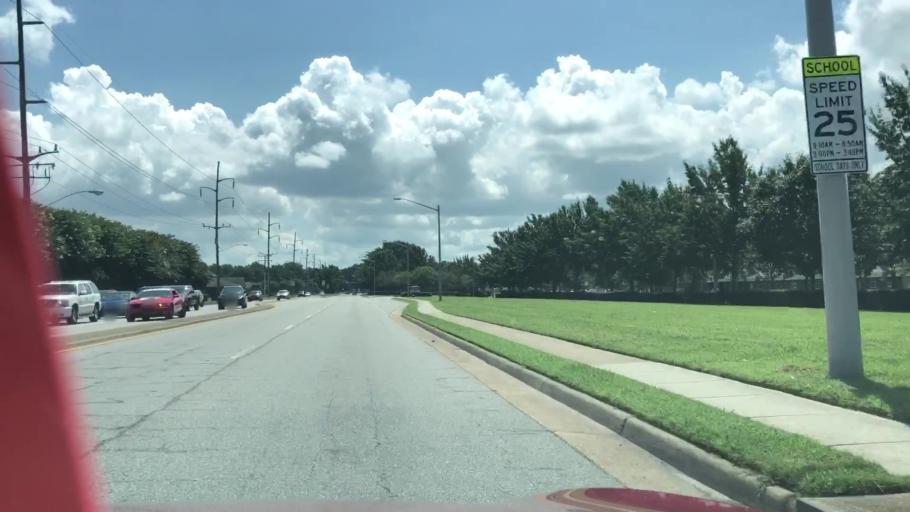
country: US
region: Virginia
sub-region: City of Virginia Beach
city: Virginia Beach
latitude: 36.8610
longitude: -76.0271
